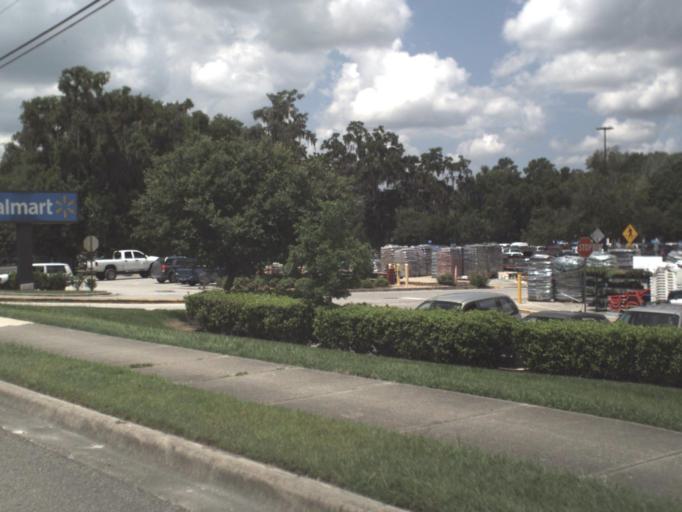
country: US
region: Florida
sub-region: Hernando County
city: South Brooksville
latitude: 28.5365
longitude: -82.4061
